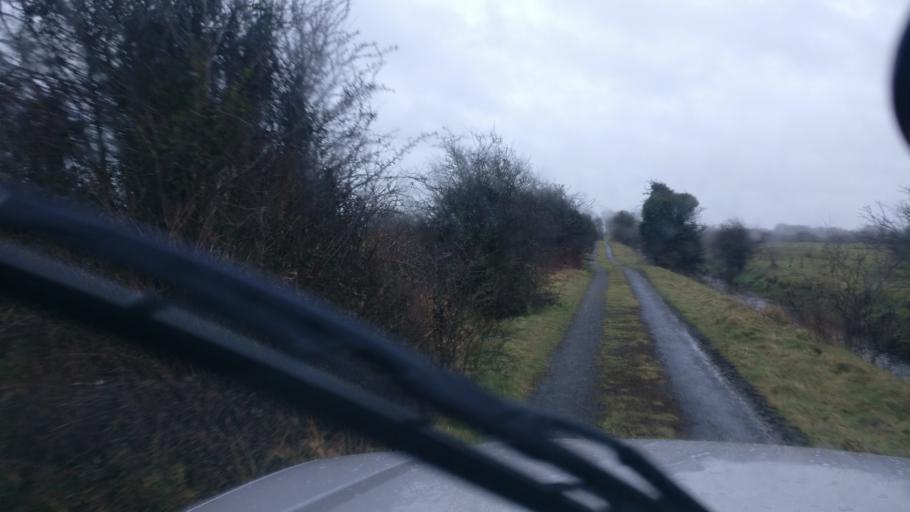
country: IE
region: Connaught
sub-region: County Galway
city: Ballinasloe
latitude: 53.2440
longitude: -8.3396
